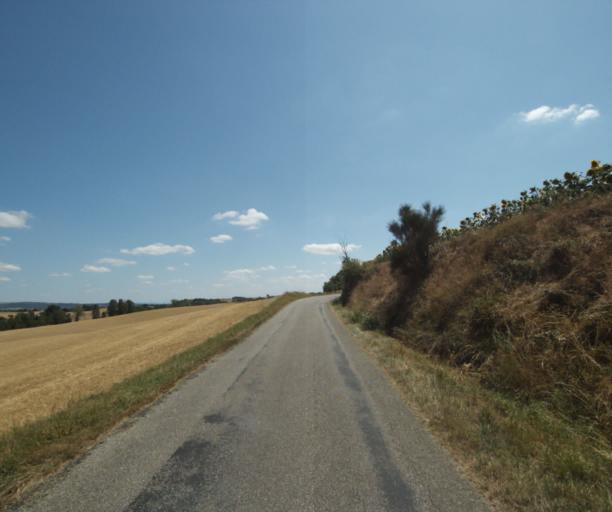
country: FR
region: Midi-Pyrenees
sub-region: Departement de la Haute-Garonne
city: Saint-Felix-Lauragais
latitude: 43.4582
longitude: 1.8929
